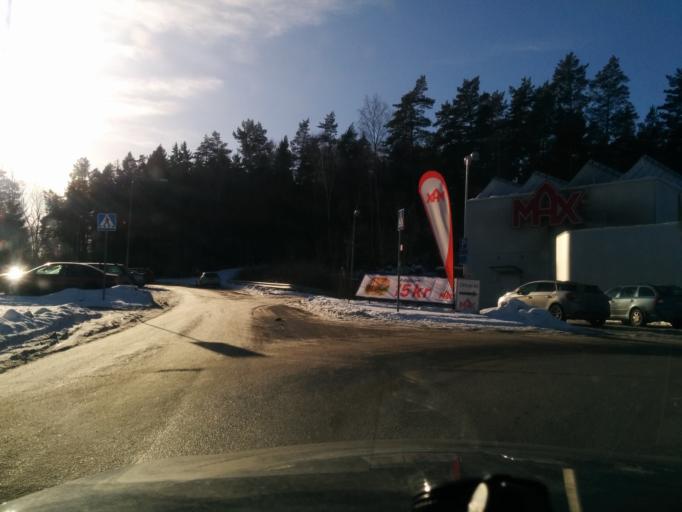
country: SE
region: Stockholm
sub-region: Taby Kommun
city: Taby
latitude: 59.4605
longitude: 18.1294
